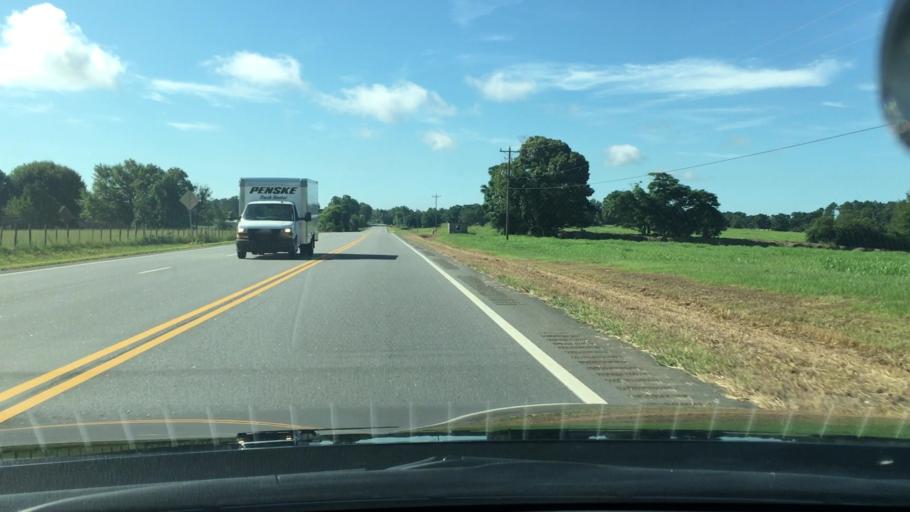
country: US
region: Georgia
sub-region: Morgan County
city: Madison
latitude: 33.4839
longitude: -83.4362
